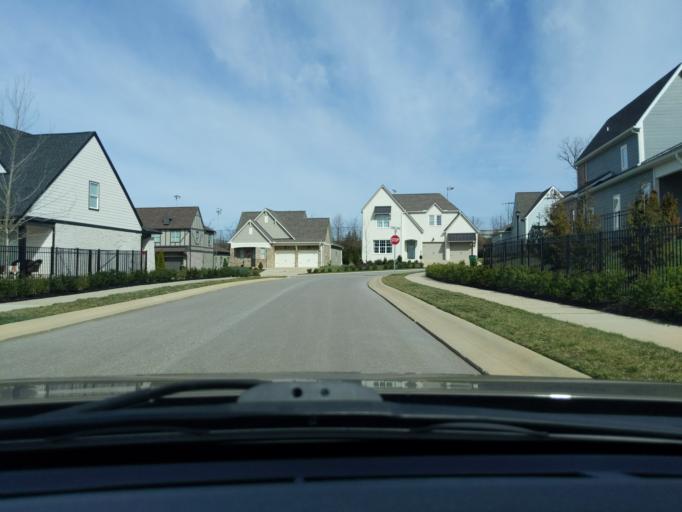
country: US
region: Tennessee
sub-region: Wilson County
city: Mount Juliet
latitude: 36.2135
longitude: -86.4919
